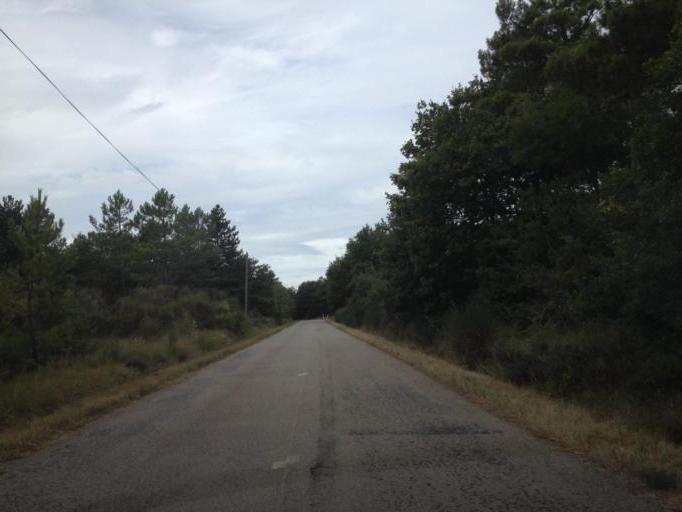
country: FR
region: Rhone-Alpes
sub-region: Departement de la Drome
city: Allan
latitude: 44.4732
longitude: 4.8175
